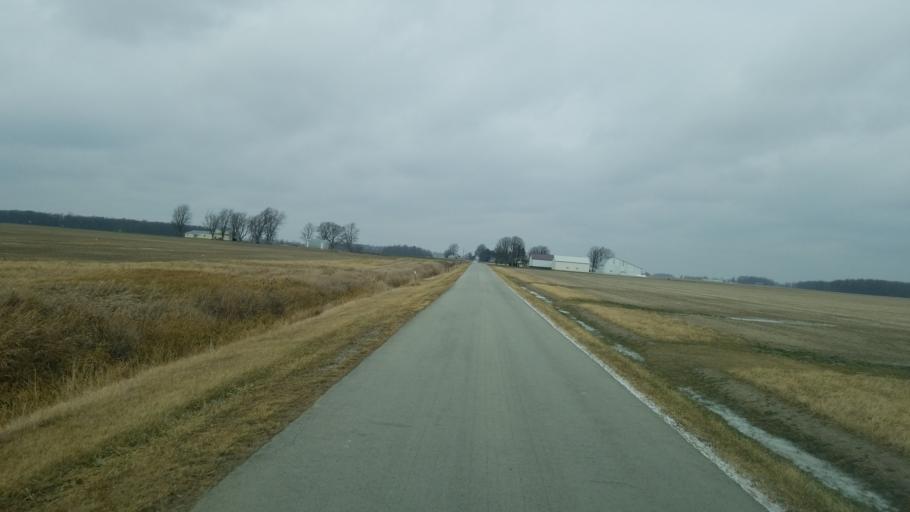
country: US
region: Ohio
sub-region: Hardin County
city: Forest
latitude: 40.7555
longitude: -83.4777
